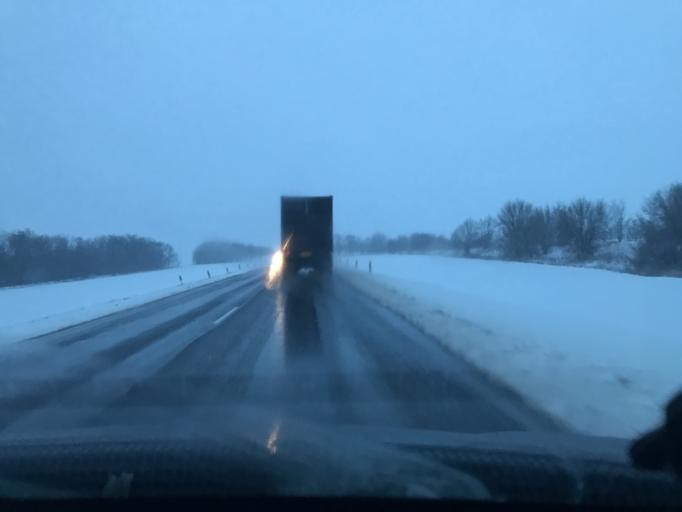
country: RU
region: Rostov
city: Letnik
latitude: 46.0364
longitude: 41.2110
